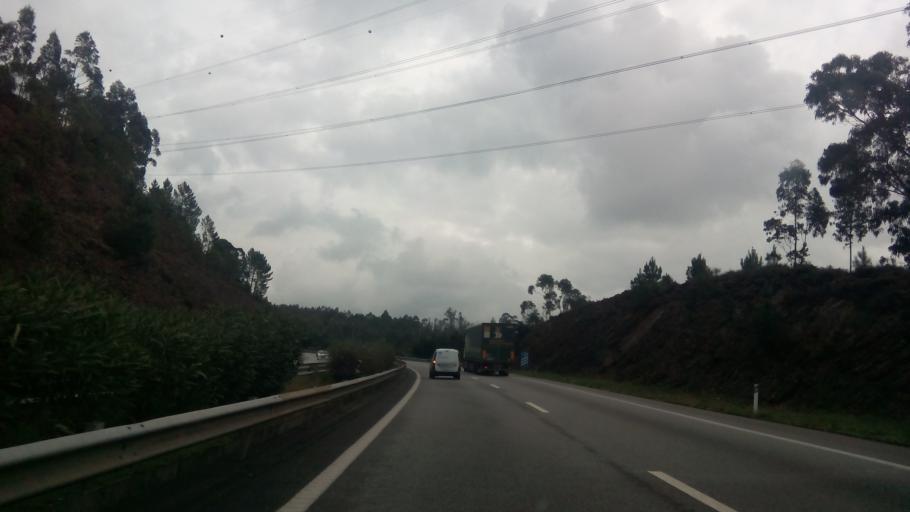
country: PT
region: Porto
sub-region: Paredes
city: Recarei
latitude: 41.1651
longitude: -8.3998
